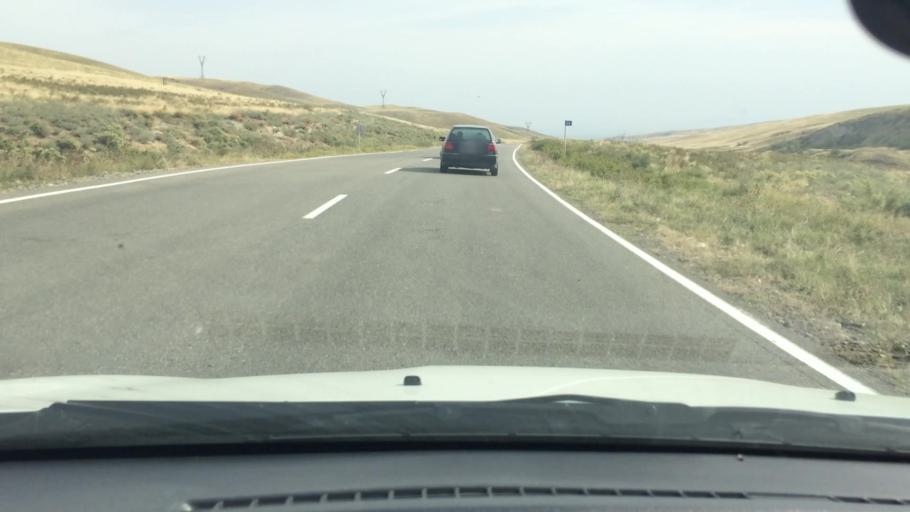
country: GE
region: Kvemo Kartli
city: Rust'avi
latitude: 41.5190
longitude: 44.9409
